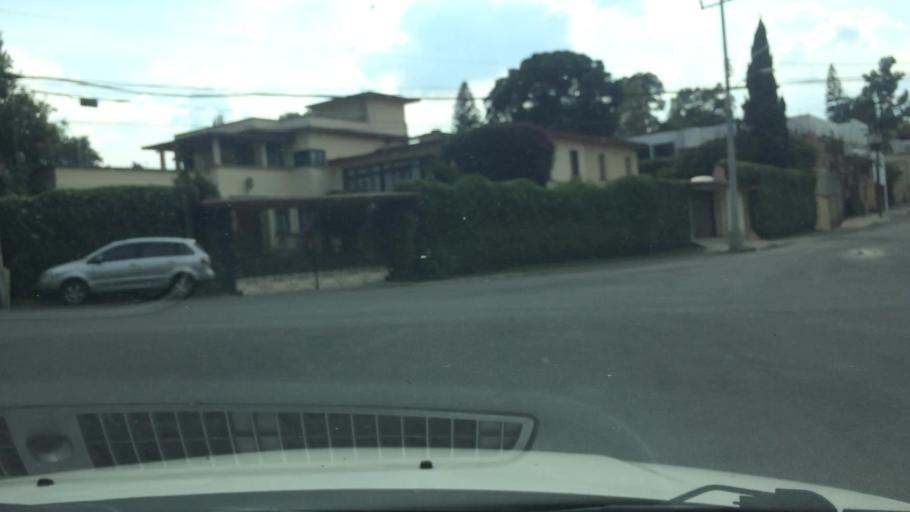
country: MX
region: Mexico City
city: Magdalena Contreras
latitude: 19.3195
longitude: -99.2138
